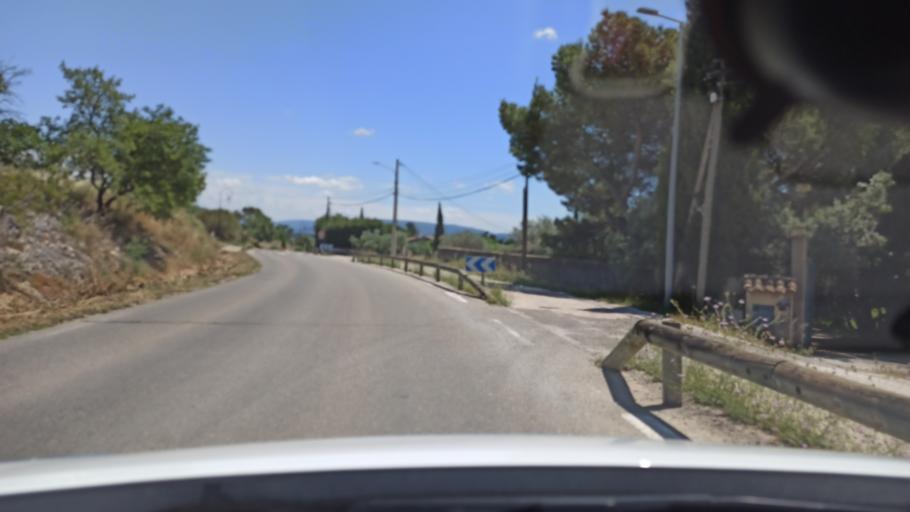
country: FR
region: Provence-Alpes-Cote d'Azur
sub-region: Departement du Vaucluse
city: Caumont-sur-Durance
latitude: 43.8962
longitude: 4.9403
